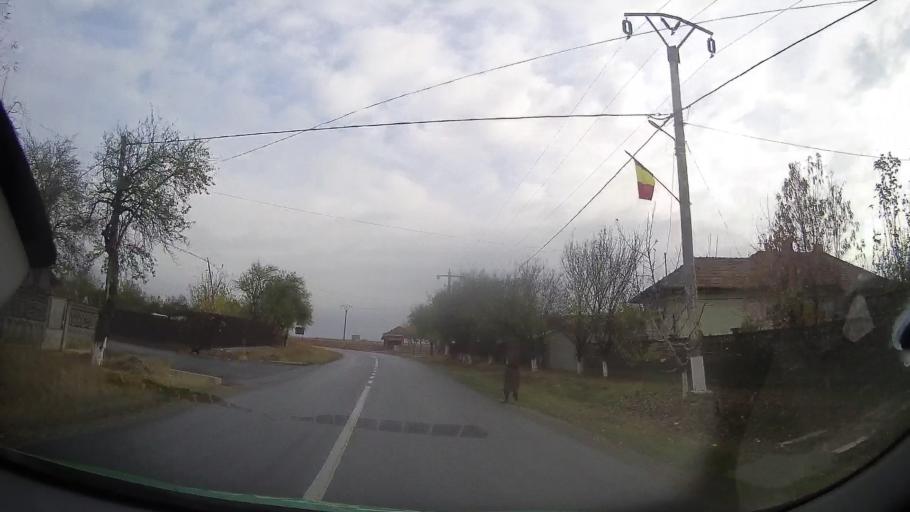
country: RO
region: Ialomita
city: Brazii
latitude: 44.7575
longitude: 26.3695
